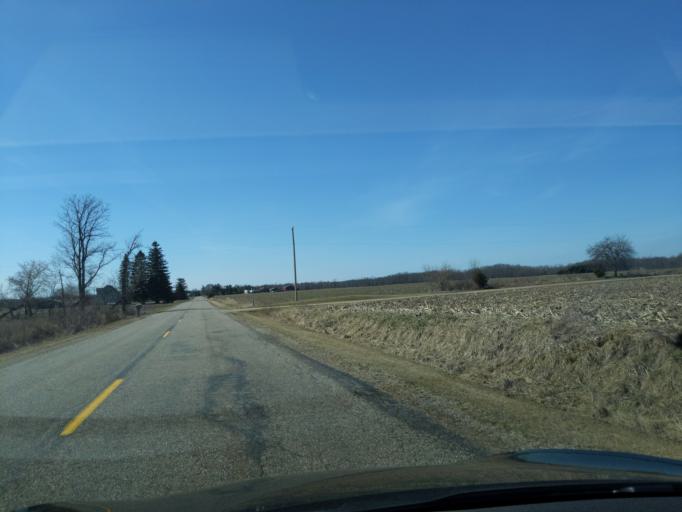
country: US
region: Michigan
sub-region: Ionia County
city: Lake Odessa
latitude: 42.7125
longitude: -85.0579
